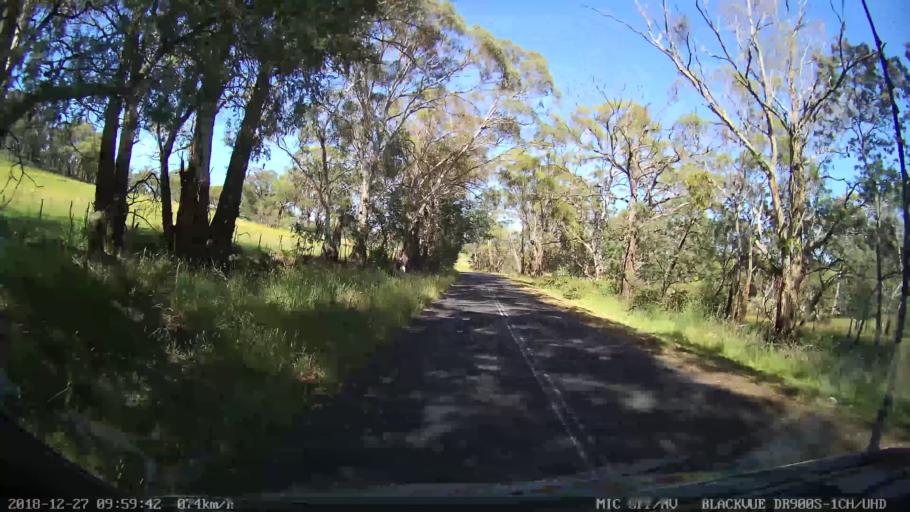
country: AU
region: New South Wales
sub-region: Lithgow
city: Portland
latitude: -33.4351
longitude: 149.9487
